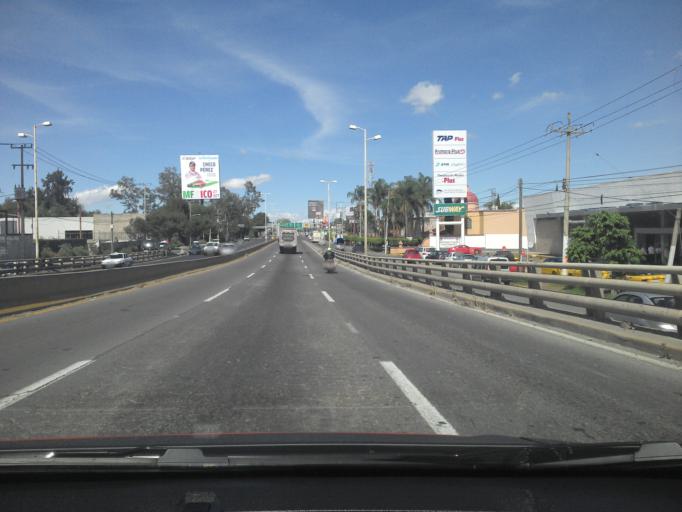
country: MX
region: Jalisco
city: Nuevo Mexico
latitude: 20.7031
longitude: -103.4612
